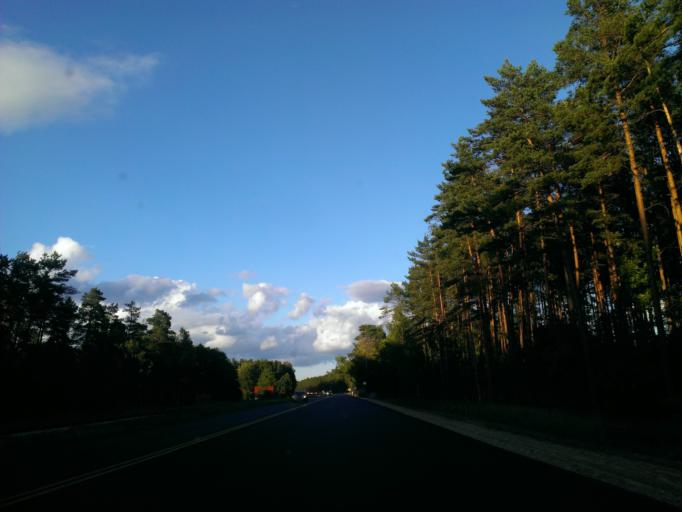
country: LV
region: Garkalne
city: Garkalne
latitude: 57.0457
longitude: 24.4337
